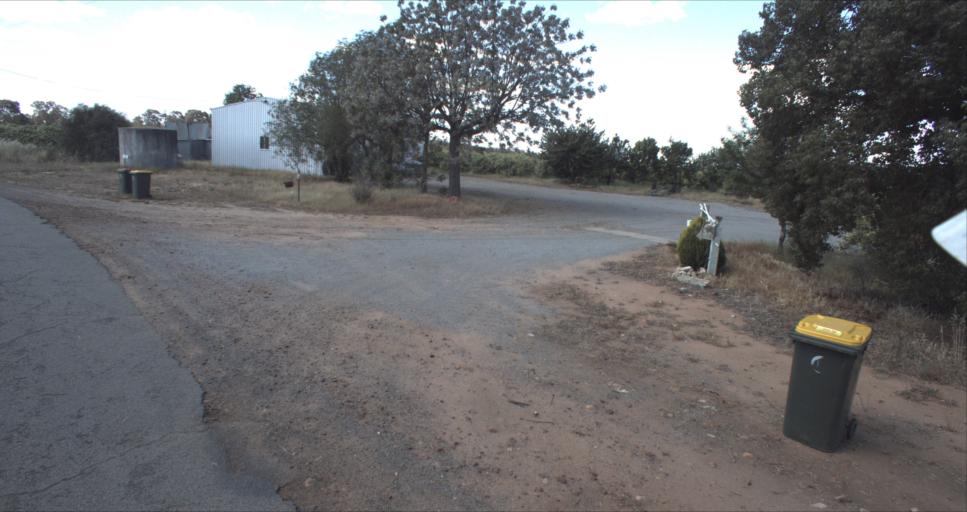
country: AU
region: New South Wales
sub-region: Leeton
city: Leeton
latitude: -34.5111
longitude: 146.2320
